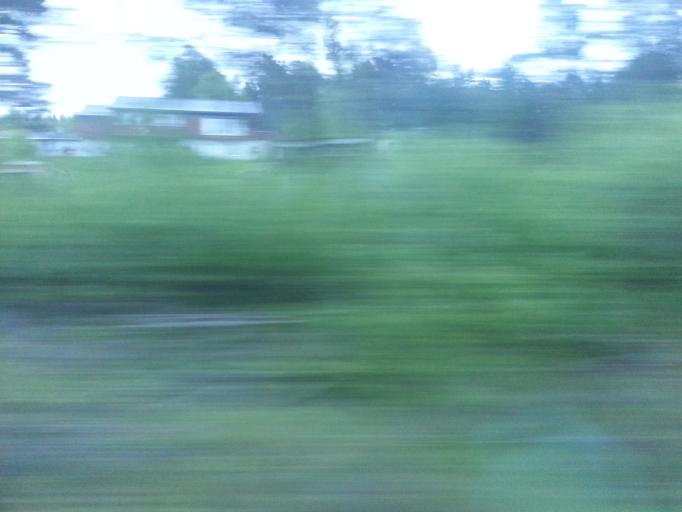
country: NO
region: Oppland
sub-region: Dovre
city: Dombas
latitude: 62.0795
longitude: 9.1354
